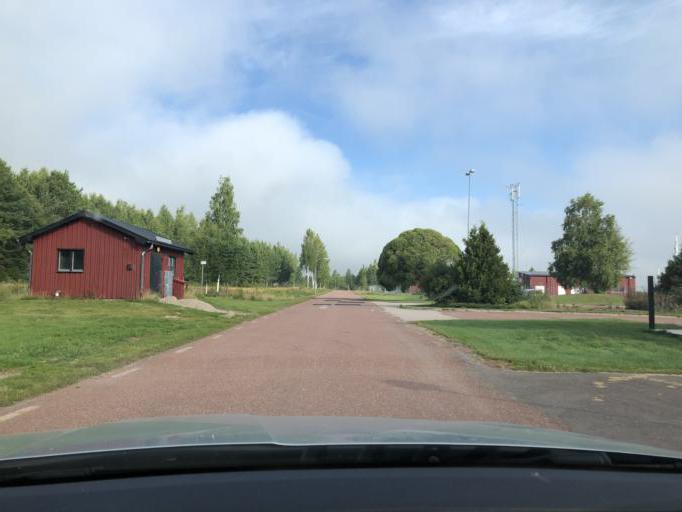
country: SE
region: Dalarna
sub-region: Mora Kommun
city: Mora
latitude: 60.9582
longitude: 14.5038
